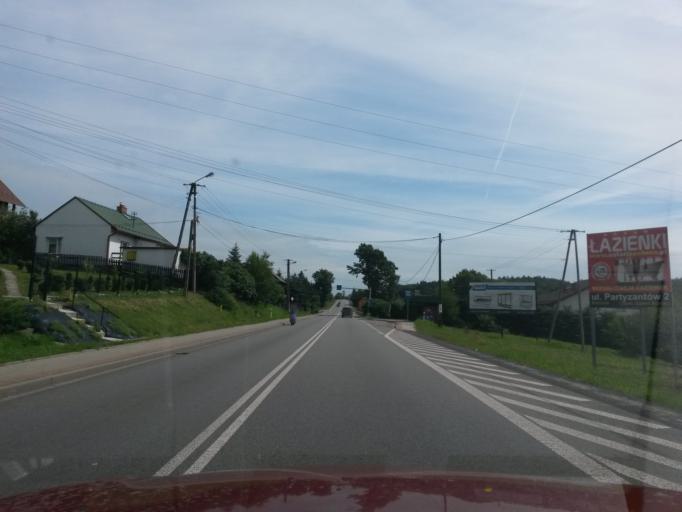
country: PL
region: Lesser Poland Voivodeship
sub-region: Powiat bochenski
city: Lapczyca
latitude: 49.9598
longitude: 20.3859
